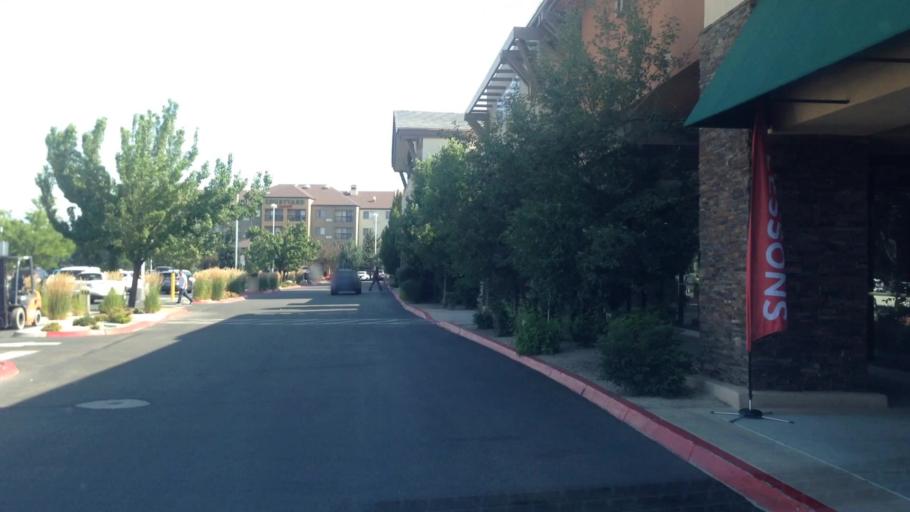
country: US
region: Nevada
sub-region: Washoe County
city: Reno
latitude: 39.4660
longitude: -119.7854
